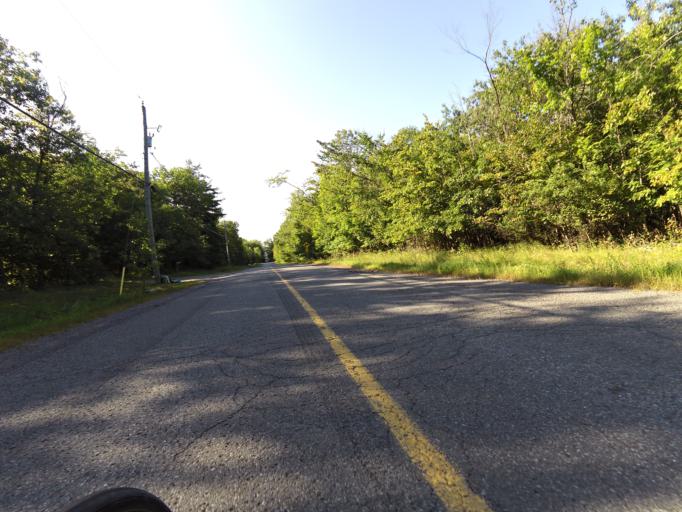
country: CA
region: Ontario
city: Bells Corners
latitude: 45.4832
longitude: -76.0475
